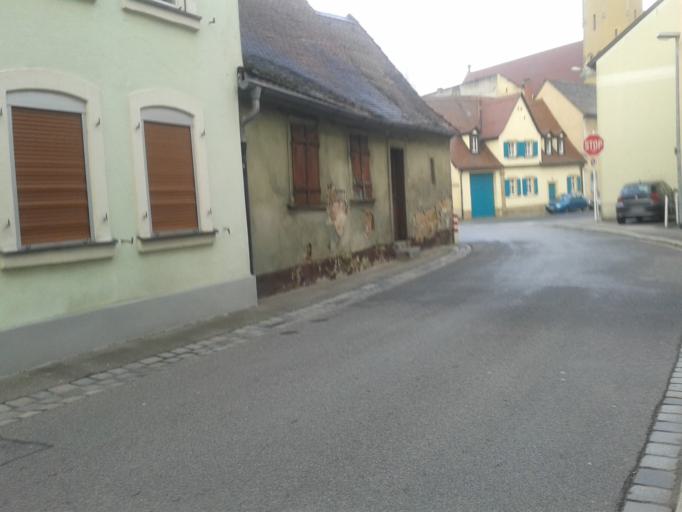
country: DE
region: Bavaria
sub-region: Upper Franconia
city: Bamberg
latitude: 49.9005
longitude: 10.8897
